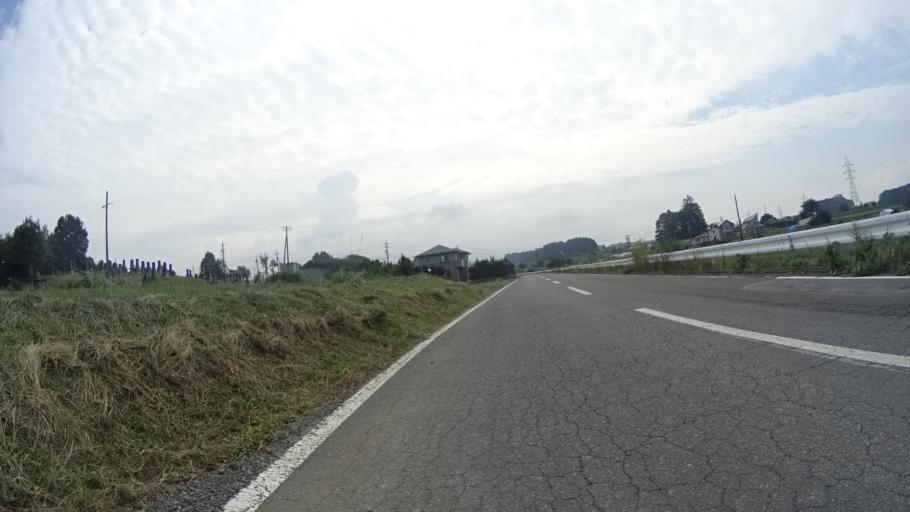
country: JP
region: Nagano
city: Chino
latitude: 35.9664
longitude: 138.1957
